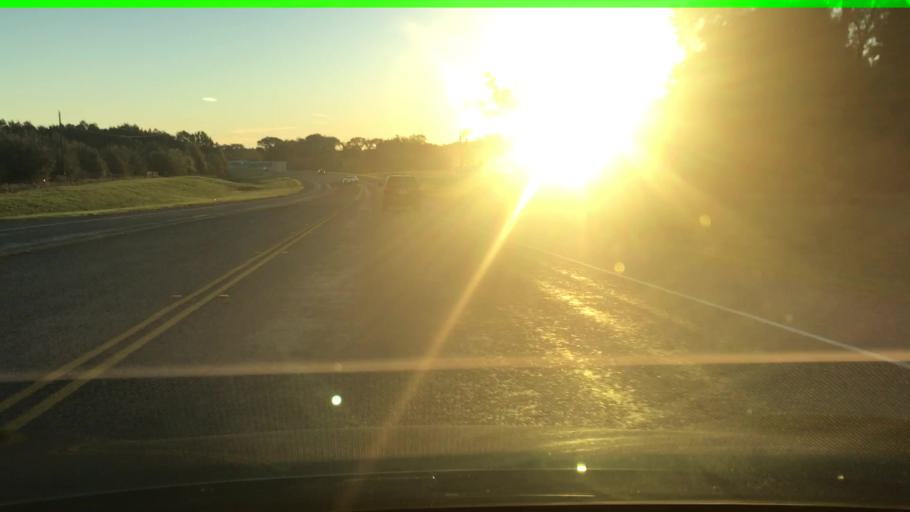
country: US
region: Texas
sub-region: Henderson County
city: Athens
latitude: 32.1714
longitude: -95.8324
